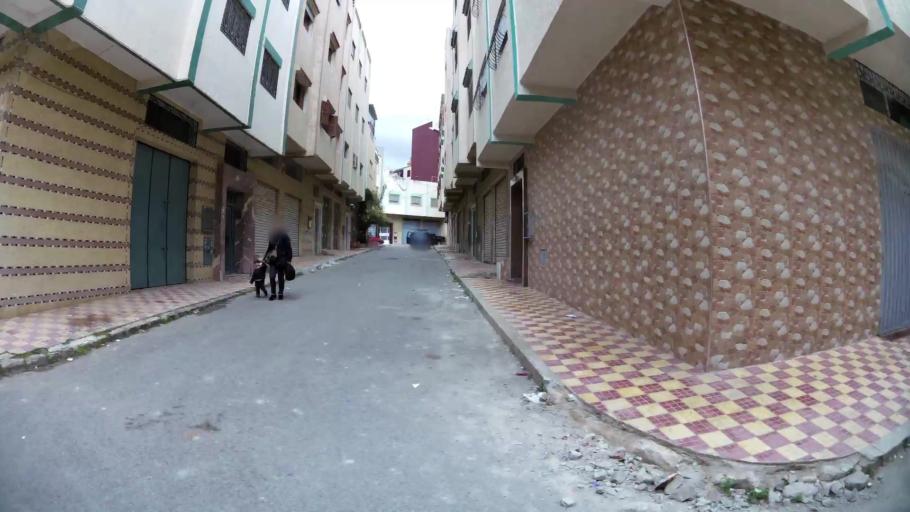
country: MA
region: Tanger-Tetouan
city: Tetouan
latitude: 35.5628
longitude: -5.3590
